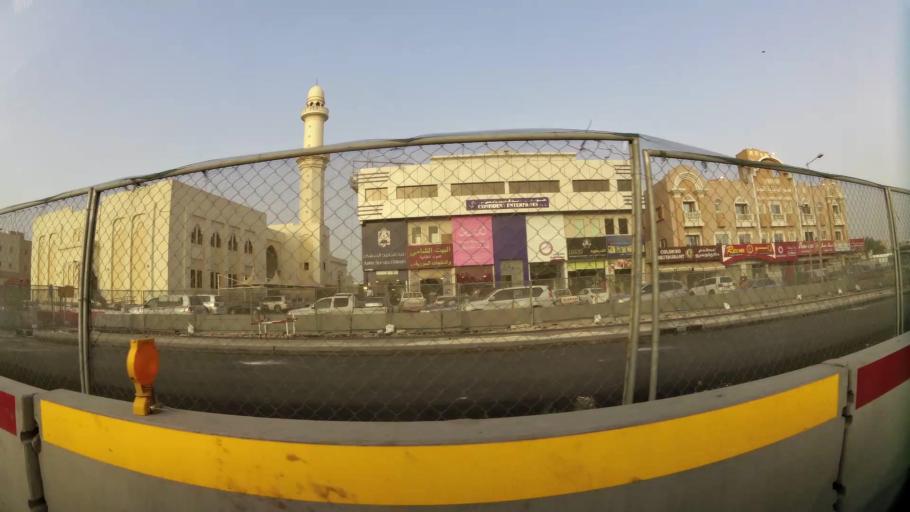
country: QA
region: Baladiyat ar Rayyan
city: Ar Rayyan
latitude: 25.2445
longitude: 51.4540
